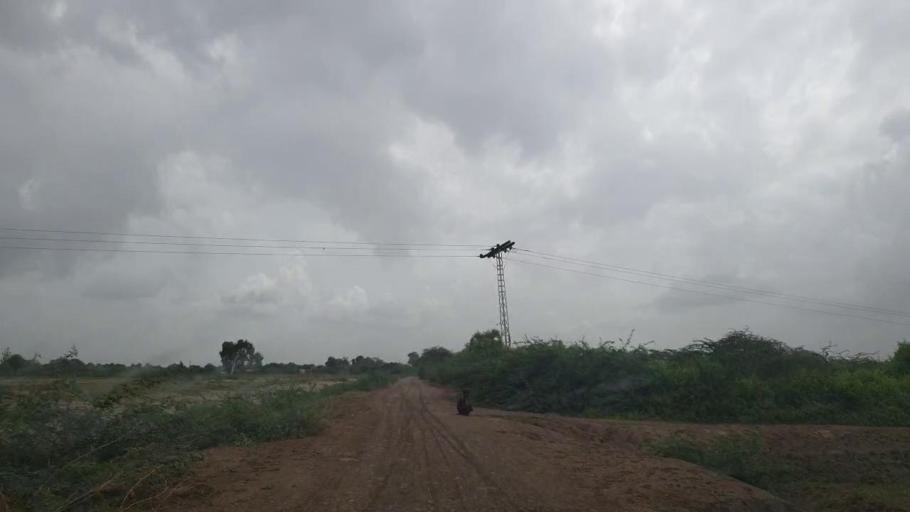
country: PK
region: Sindh
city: Naukot
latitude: 24.8787
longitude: 69.2440
